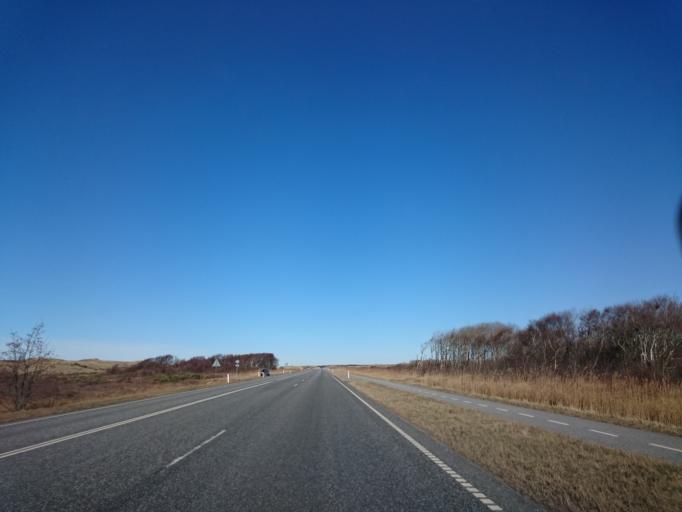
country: DK
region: North Denmark
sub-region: Frederikshavn Kommune
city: Skagen
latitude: 57.6738
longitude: 10.4564
